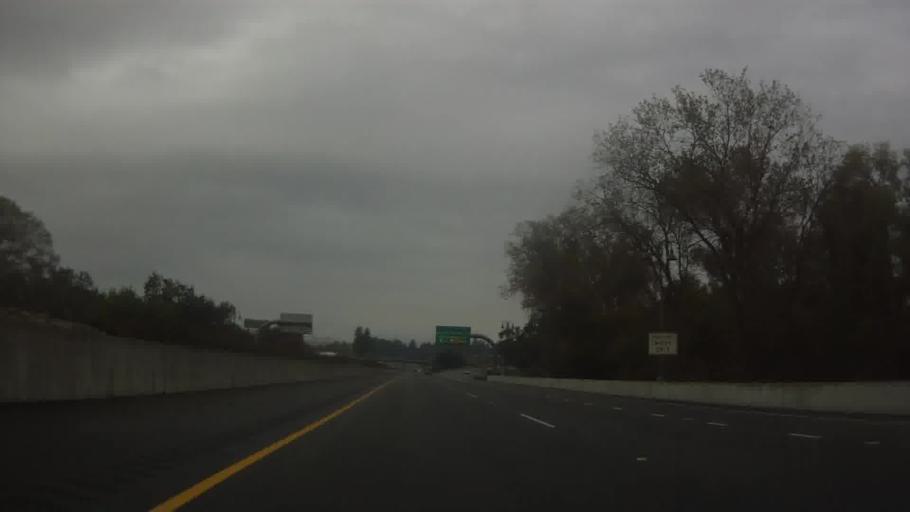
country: US
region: California
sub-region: Shasta County
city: Redding
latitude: 40.5863
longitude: -122.3734
